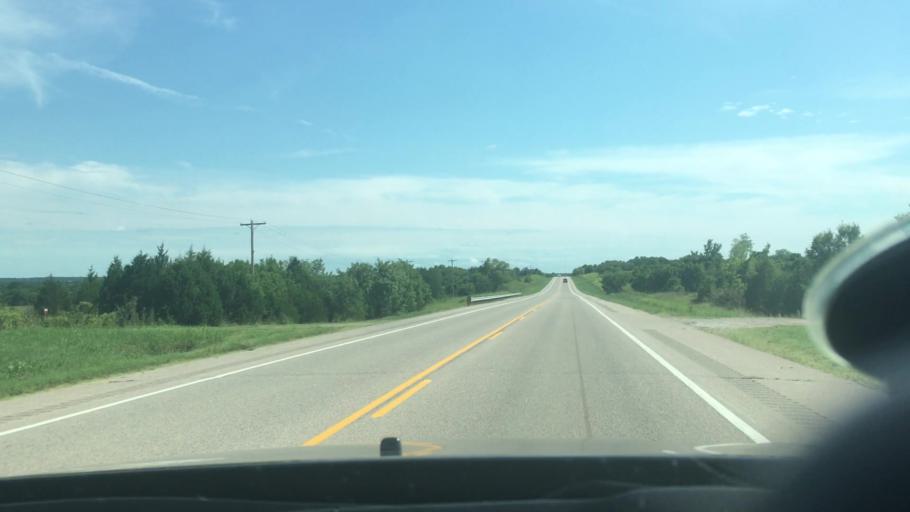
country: US
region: Oklahoma
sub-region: Seminole County
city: Konawa
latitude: 34.9831
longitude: -96.6793
